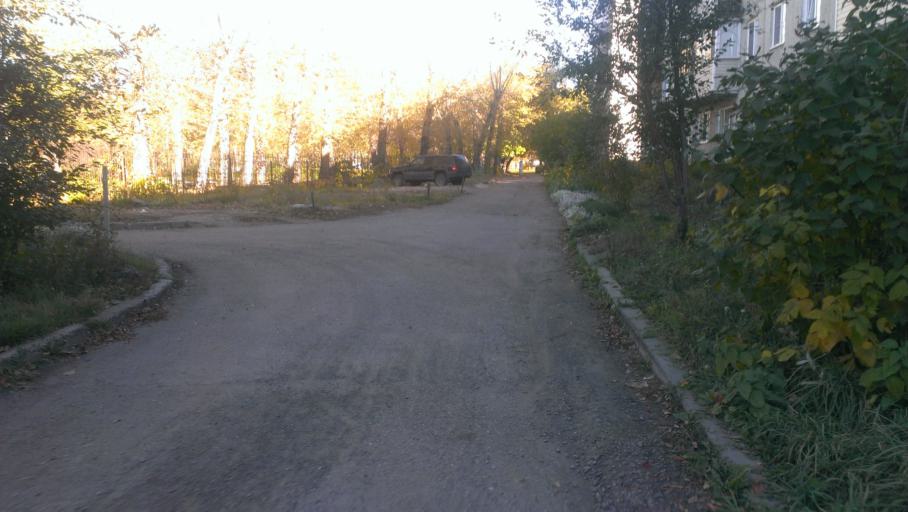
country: RU
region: Altai Krai
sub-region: Gorod Barnaulskiy
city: Barnaul
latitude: 53.3648
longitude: 83.6846
